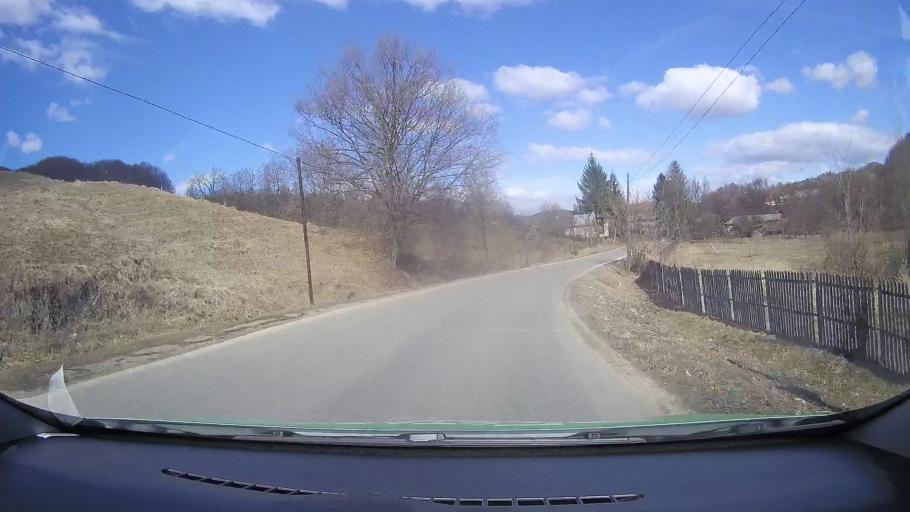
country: RO
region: Dambovita
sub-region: Comuna Vulcana Bai
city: Vulcana Bai
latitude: 45.0627
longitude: 25.3776
